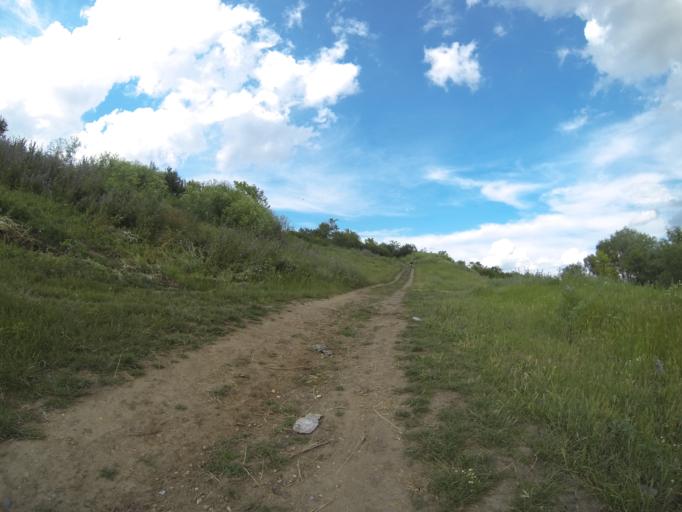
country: RO
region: Dolj
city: Satu Nou Calopar
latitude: 44.1271
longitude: 23.7921
